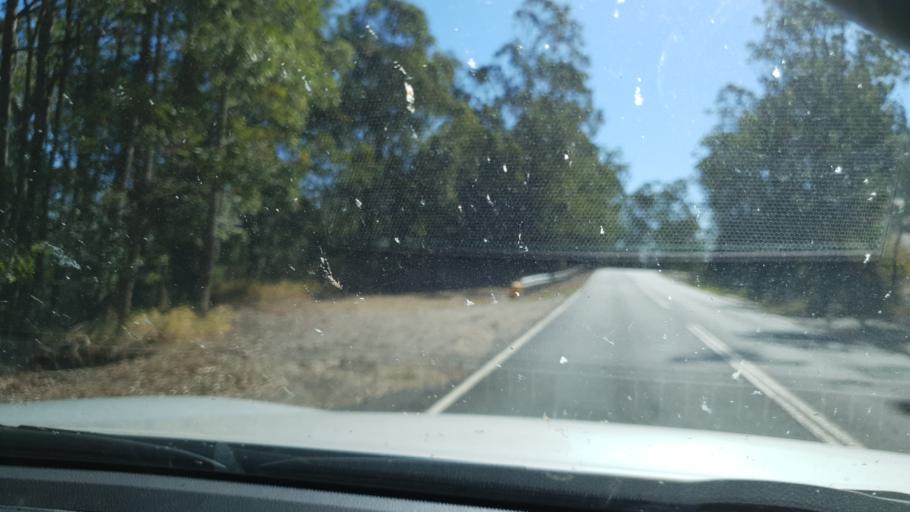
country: AU
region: Queensland
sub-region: Moreton Bay
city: Samford Valley
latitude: -27.3313
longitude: 152.9165
